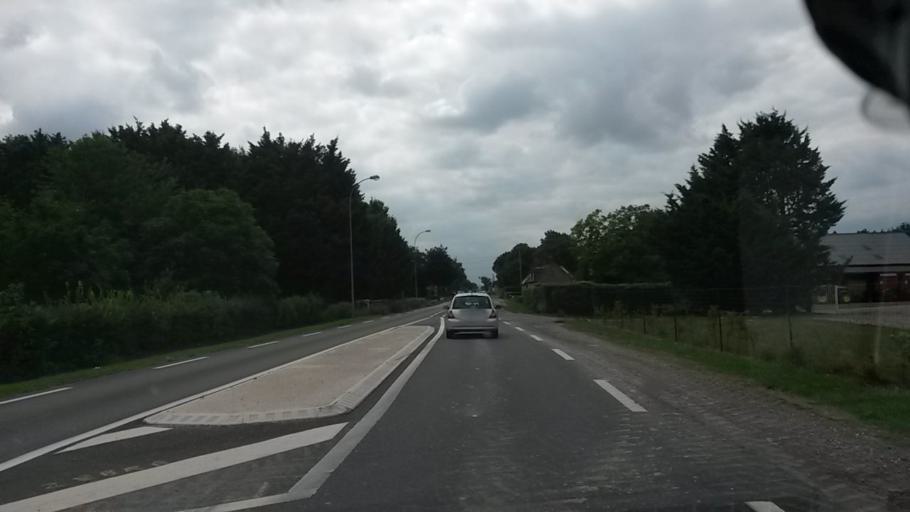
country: FR
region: Picardie
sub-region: Departement de la Somme
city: Camon
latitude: 49.9217
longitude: 2.3717
